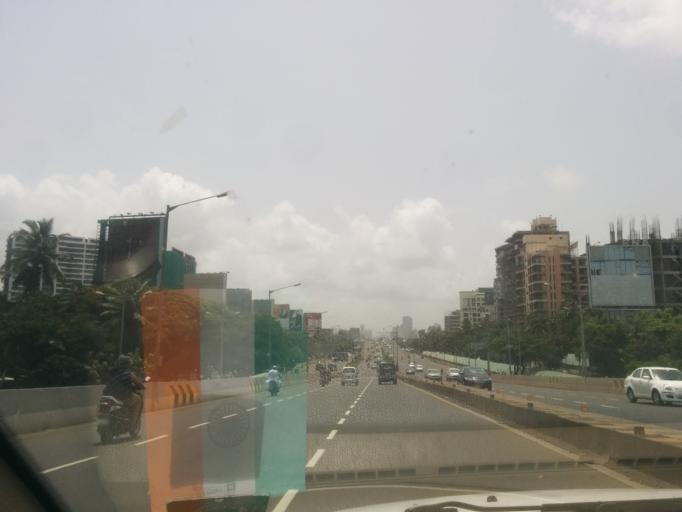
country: IN
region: Maharashtra
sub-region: Mumbai Suburban
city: Mumbai
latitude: 19.0604
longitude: 72.8465
